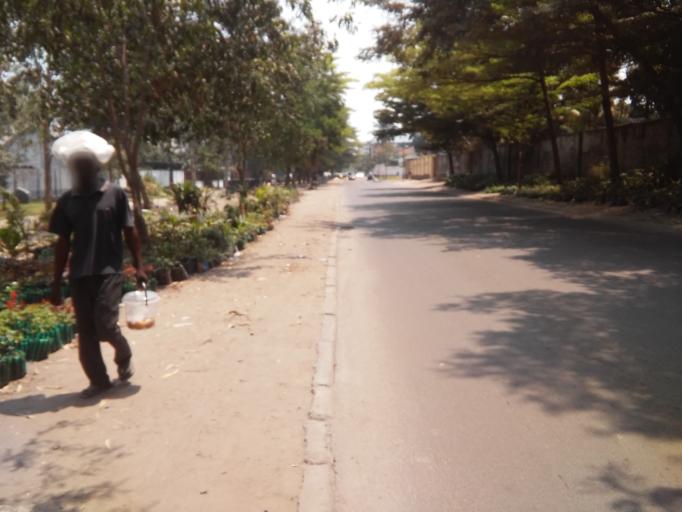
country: CD
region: Kinshasa
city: Kinshasa
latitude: -4.3184
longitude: 15.2854
